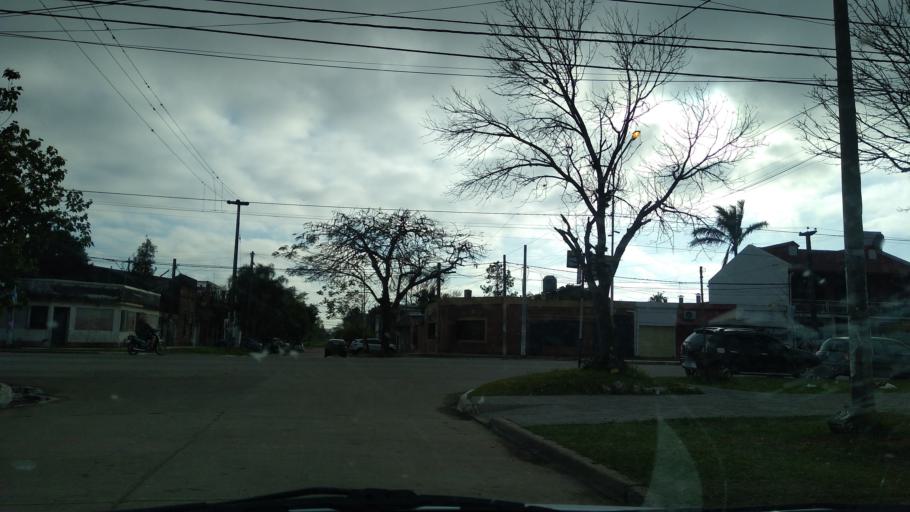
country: AR
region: Chaco
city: Barranqueras
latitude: -27.4855
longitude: -58.9337
